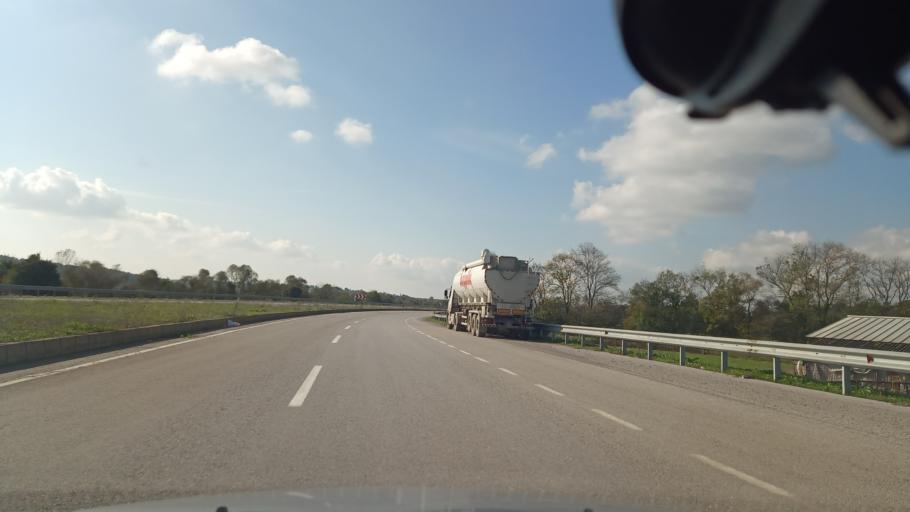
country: TR
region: Sakarya
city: Kaynarca
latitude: 41.0737
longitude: 30.3992
